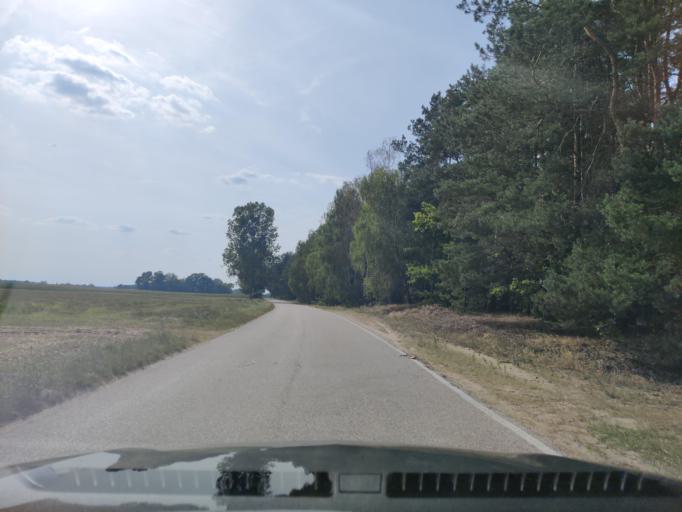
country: PL
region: Masovian Voivodeship
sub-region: Powiat wyszkowski
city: Rzasnik
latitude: 52.7660
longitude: 21.3871
